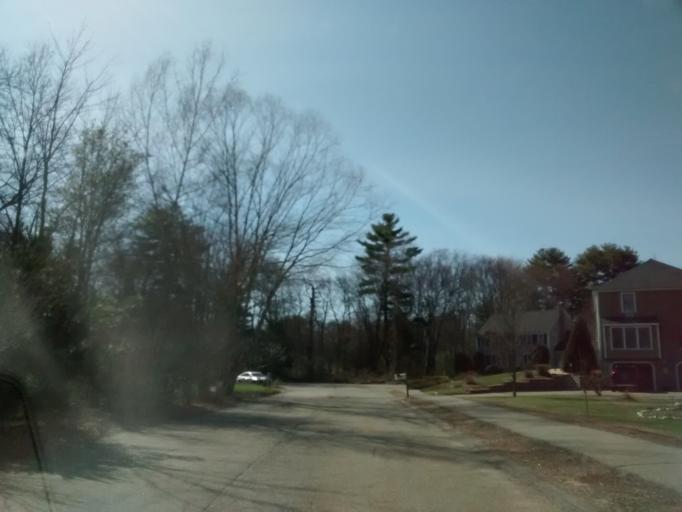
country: US
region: Massachusetts
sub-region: Norfolk County
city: Medway
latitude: 42.1562
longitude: -71.4092
